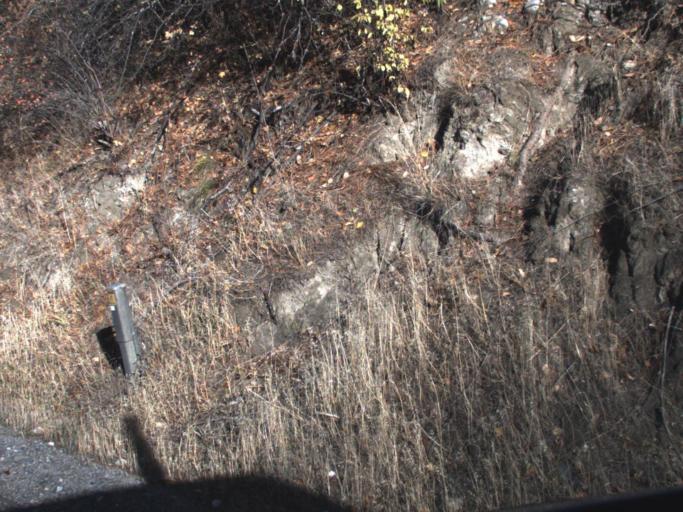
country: CA
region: British Columbia
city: Rossland
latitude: 48.8932
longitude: -117.8186
